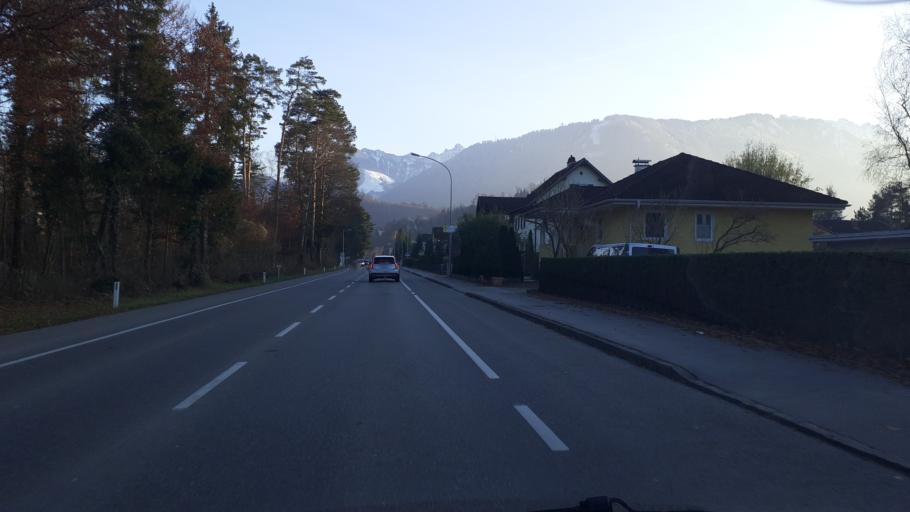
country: AT
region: Vorarlberg
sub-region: Politischer Bezirk Feldkirch
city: Nofels
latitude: 47.2482
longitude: 9.5842
